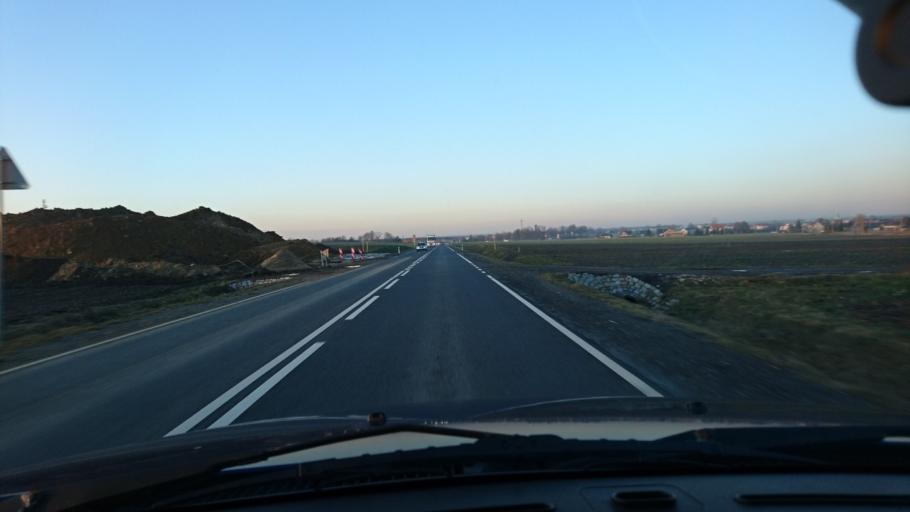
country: PL
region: Silesian Voivodeship
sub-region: Powiat gliwicki
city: Wielowies
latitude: 50.4961
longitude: 18.6070
